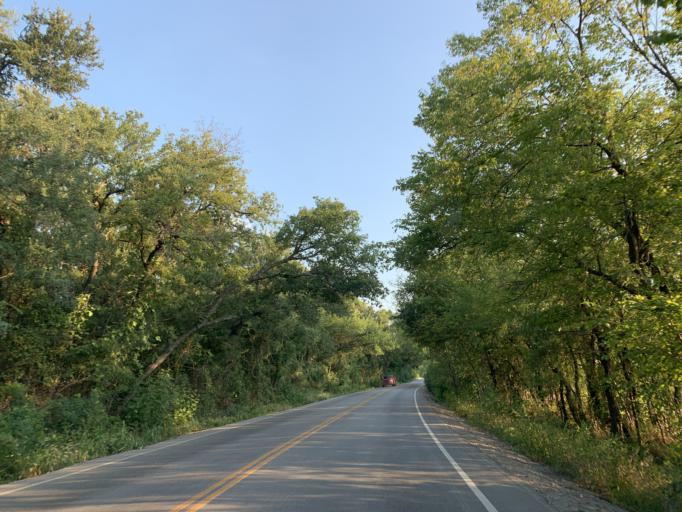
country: US
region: Texas
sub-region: Tarrant County
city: Hurst
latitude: 32.7840
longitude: -97.1779
